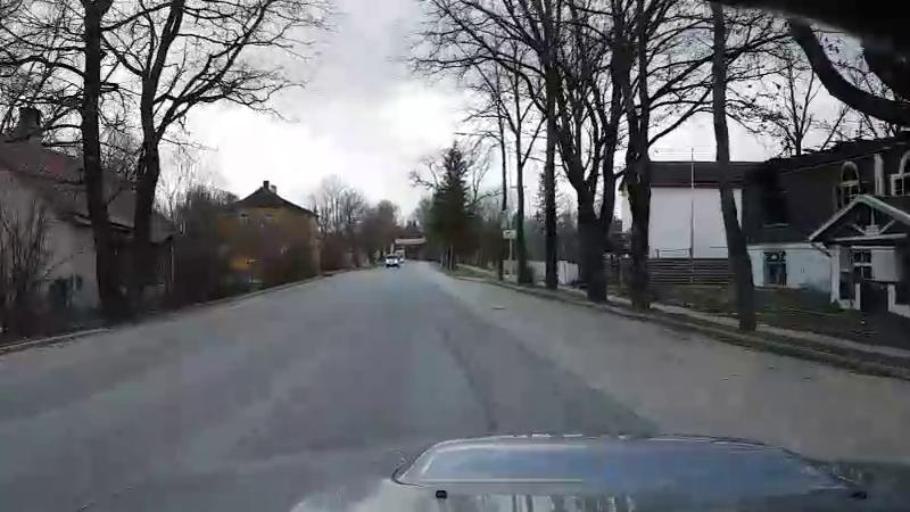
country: EE
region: Jaervamaa
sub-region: Paide linn
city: Paide
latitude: 58.8933
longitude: 25.5695
